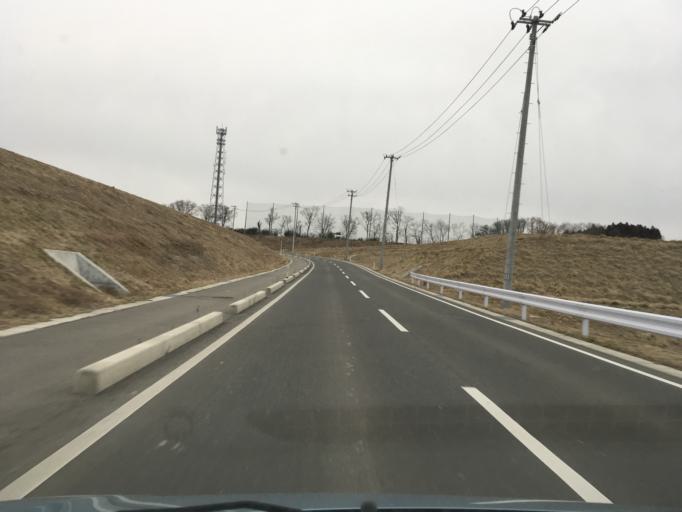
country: JP
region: Miyagi
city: Wakuya
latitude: 38.6937
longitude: 141.1710
